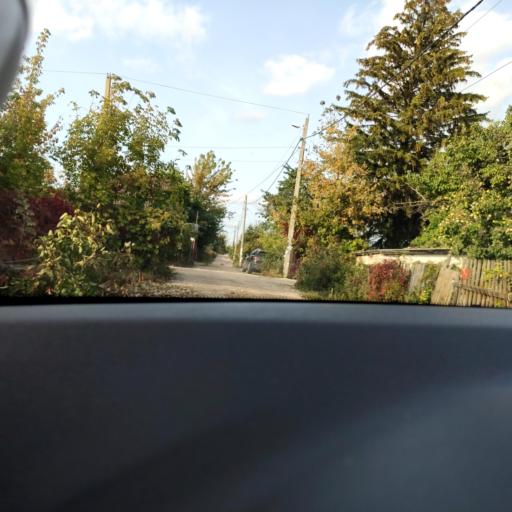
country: RU
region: Samara
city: Petra-Dubrava
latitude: 53.2781
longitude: 50.2964
